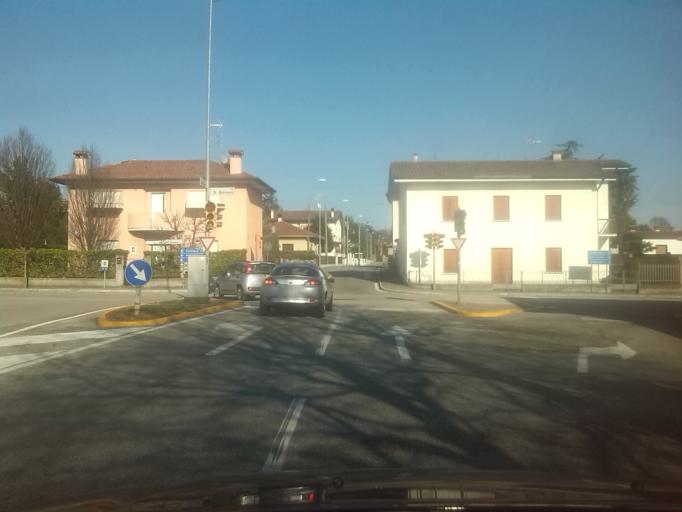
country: IT
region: Friuli Venezia Giulia
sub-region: Provincia di Udine
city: Manzano
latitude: 45.9926
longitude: 13.3923
